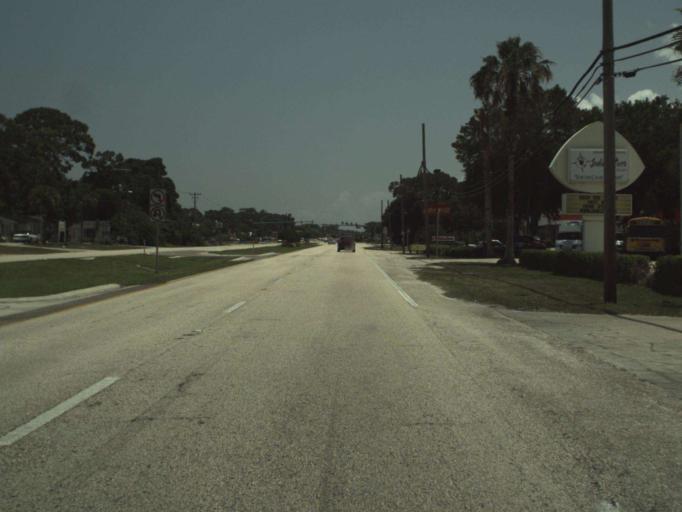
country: US
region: Florida
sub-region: Volusia County
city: Edgewater
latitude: 28.9756
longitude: -80.8978
